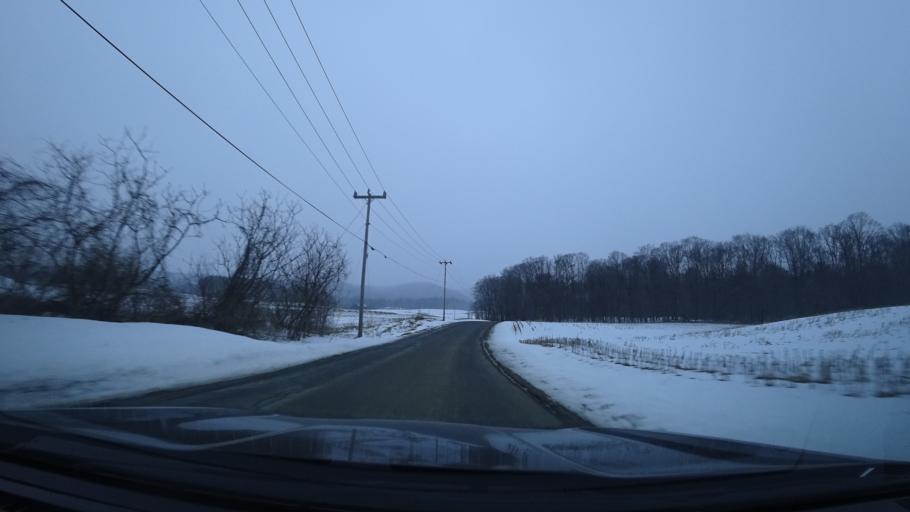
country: US
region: New York
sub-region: Washington County
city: Cambridge
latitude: 43.1580
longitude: -73.3553
